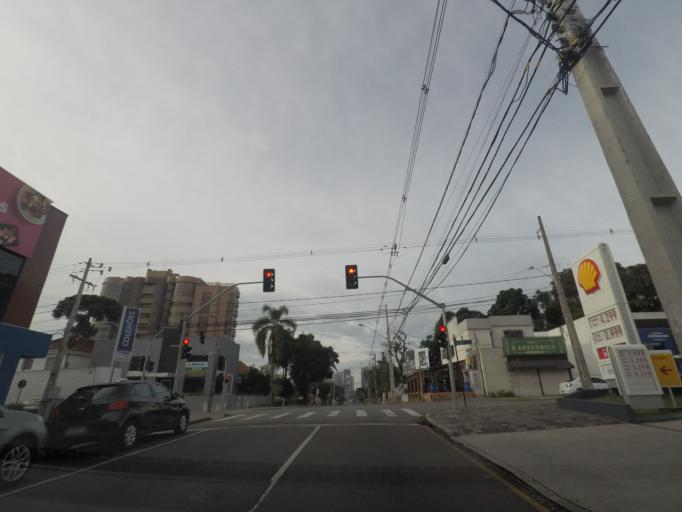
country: BR
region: Parana
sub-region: Curitiba
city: Curitiba
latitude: -25.4375
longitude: -49.2920
